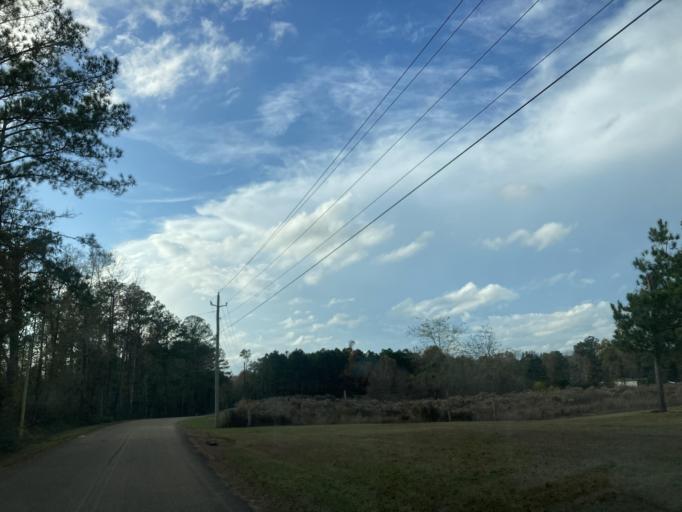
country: US
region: Mississippi
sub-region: Lamar County
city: Purvis
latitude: 31.1416
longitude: -89.6283
